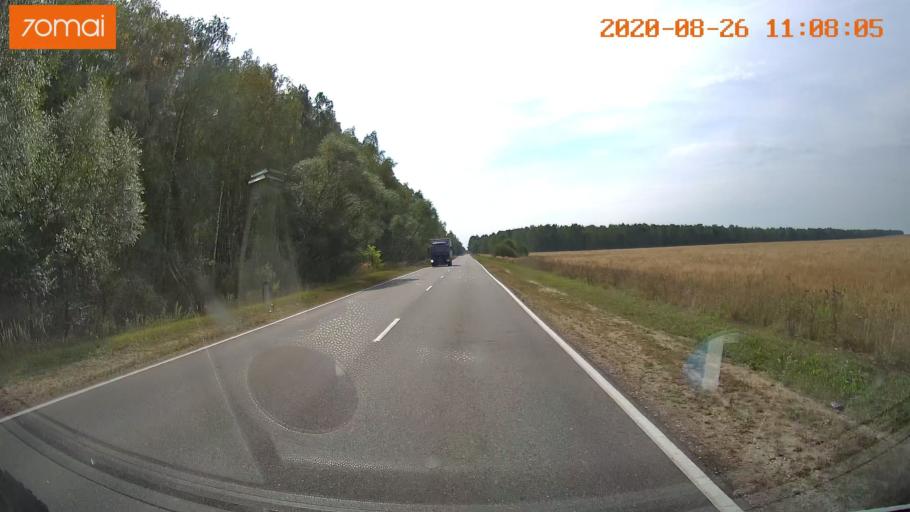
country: RU
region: Rjazan
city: Izhevskoye
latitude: 54.5099
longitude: 41.1213
